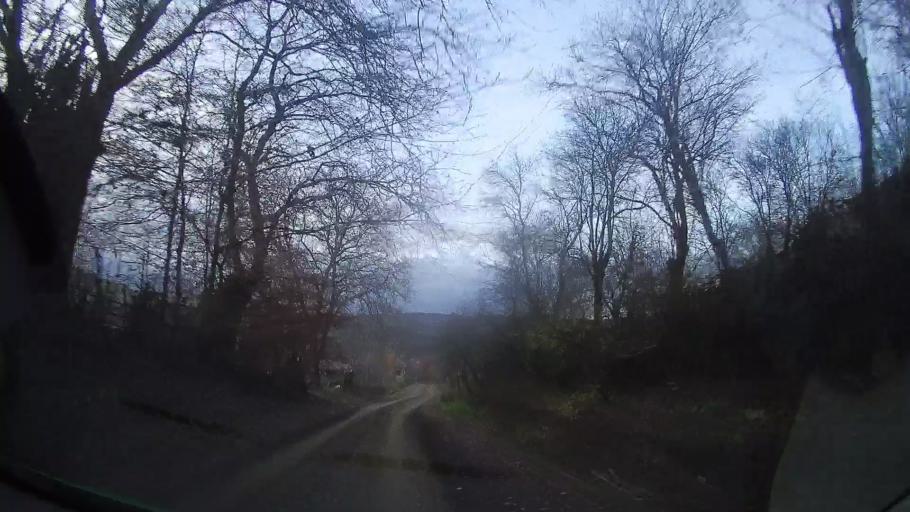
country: RO
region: Cluj
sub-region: Comuna Palatca
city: Palatca
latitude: 46.8621
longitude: 24.0237
